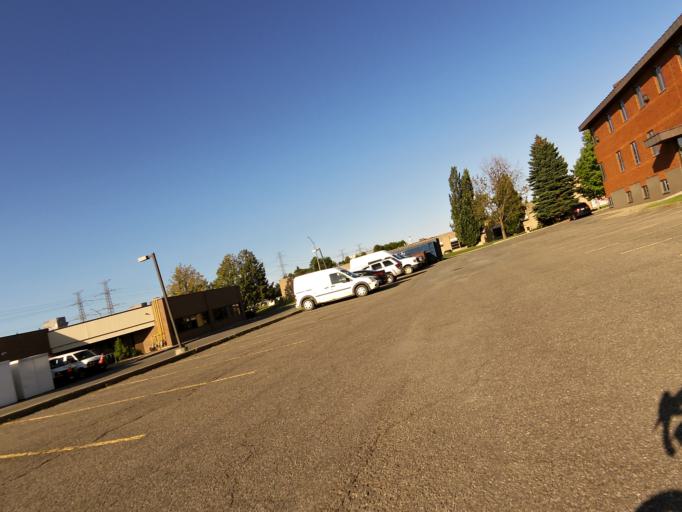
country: CA
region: Ontario
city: Ottawa
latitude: 45.3428
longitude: -75.7094
